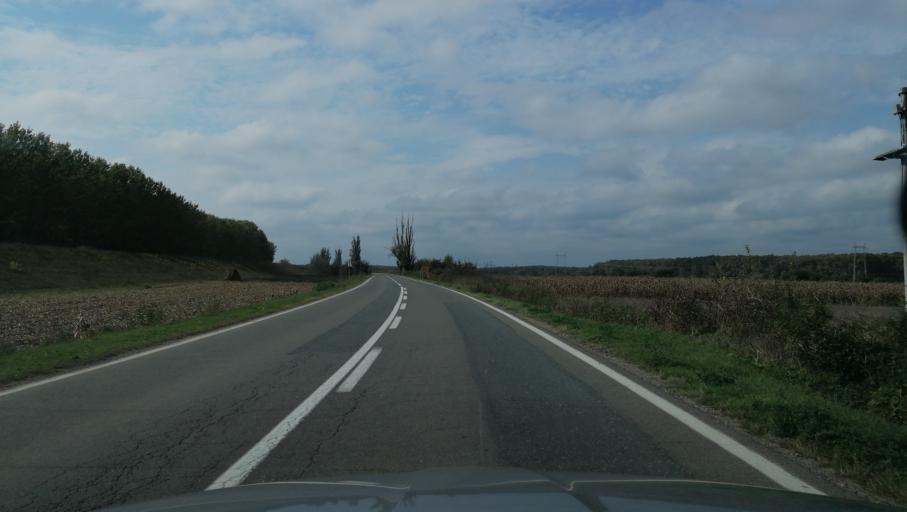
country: RS
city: Bosut
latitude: 44.9252
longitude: 19.3332
